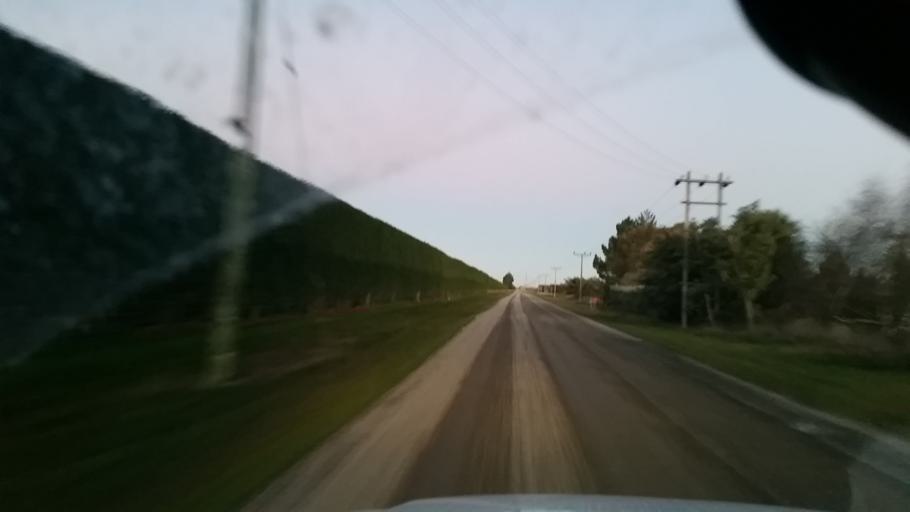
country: NZ
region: Canterbury
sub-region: Ashburton District
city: Tinwald
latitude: -43.9705
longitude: 171.6366
